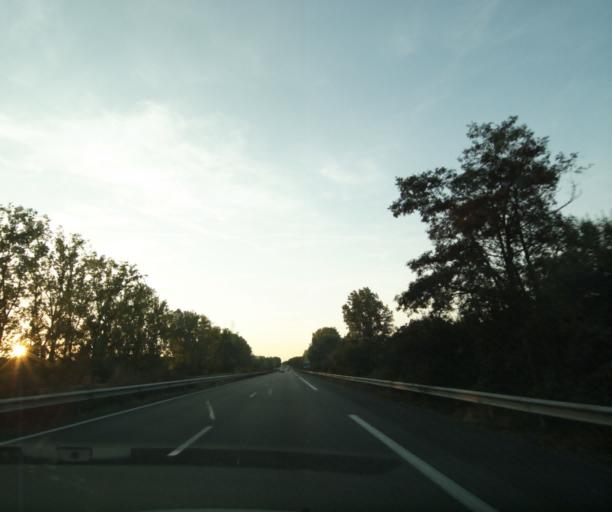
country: FR
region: Aquitaine
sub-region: Departement du Lot-et-Garonne
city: Fourques-sur-Garonne
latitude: 44.4339
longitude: 0.1279
